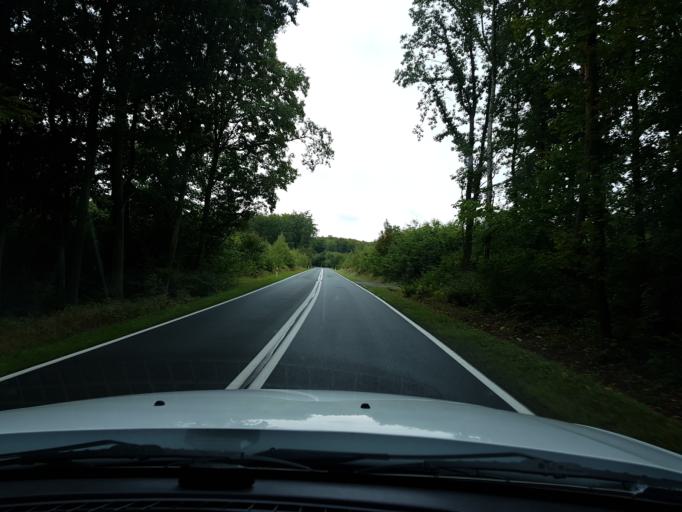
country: PL
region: West Pomeranian Voivodeship
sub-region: Powiat gryfinski
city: Widuchowa
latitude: 53.0819
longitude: 14.4286
